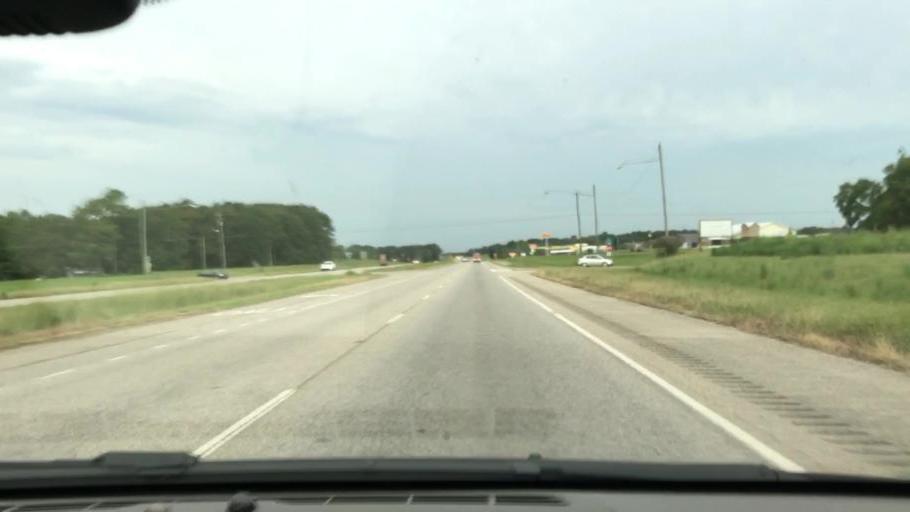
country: US
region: Alabama
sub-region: Houston County
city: Ashford
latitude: 31.1782
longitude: -85.2439
